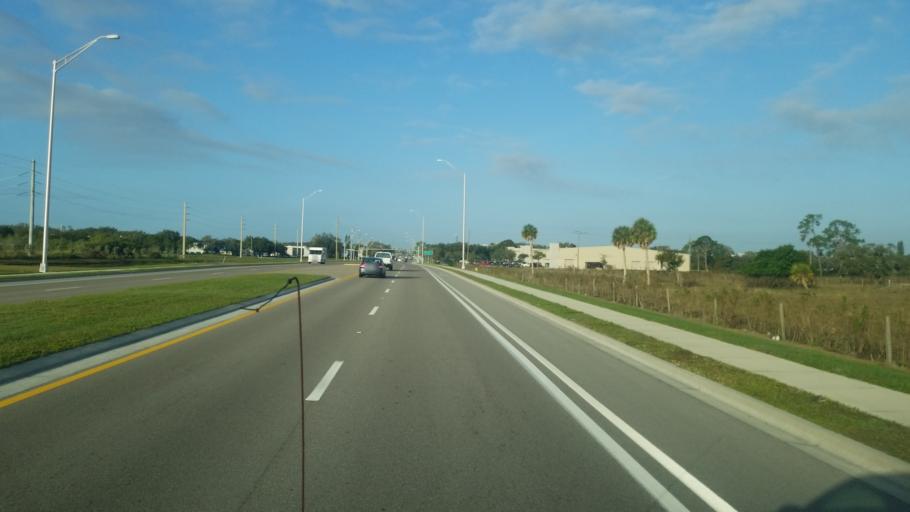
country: US
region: Florida
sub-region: Manatee County
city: Samoset
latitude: 27.4622
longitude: -82.5359
